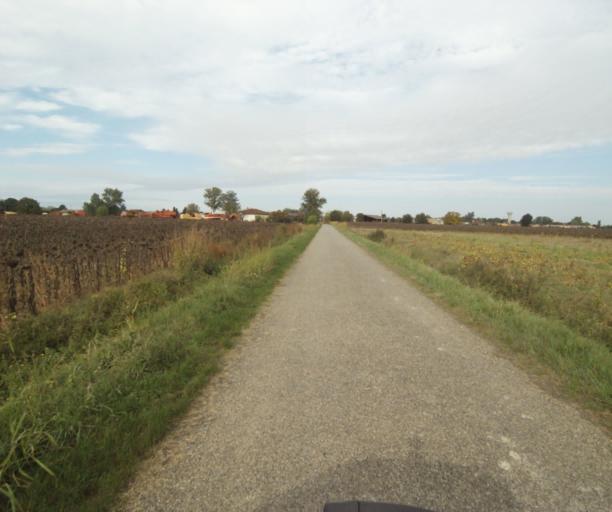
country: FR
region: Midi-Pyrenees
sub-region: Departement du Tarn-et-Garonne
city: Finhan
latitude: 43.9061
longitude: 1.2324
